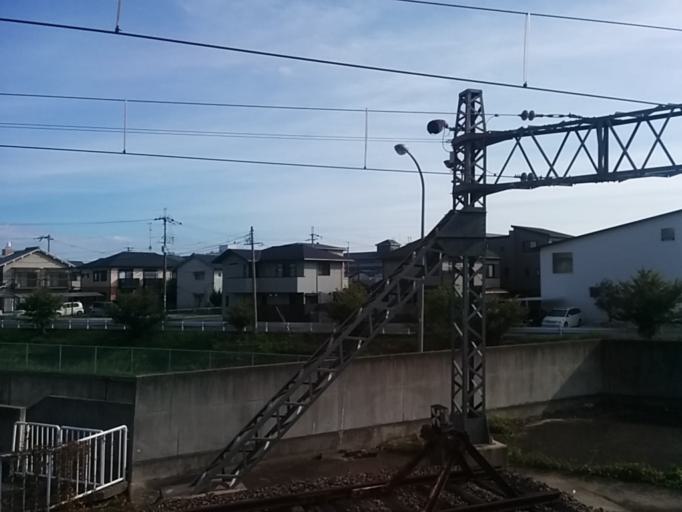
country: JP
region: Nara
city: Nara-shi
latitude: 34.6922
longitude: 135.7862
